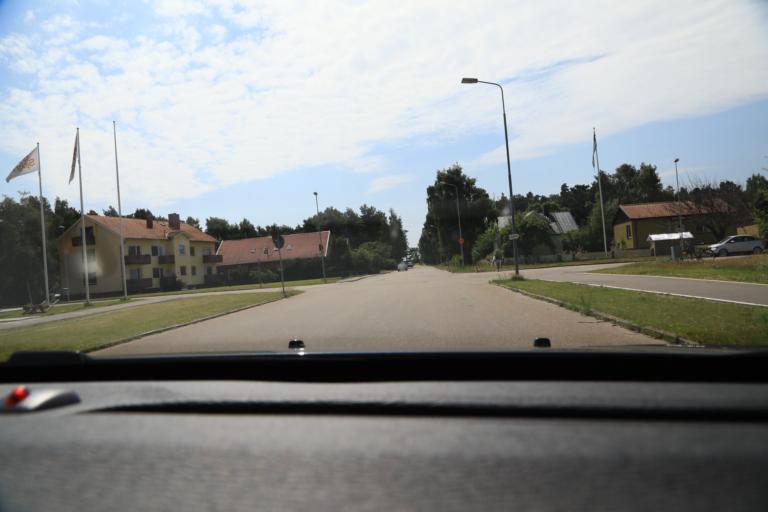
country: SE
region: Halland
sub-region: Halmstads Kommun
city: Halmstad
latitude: 56.6638
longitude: 12.8531
